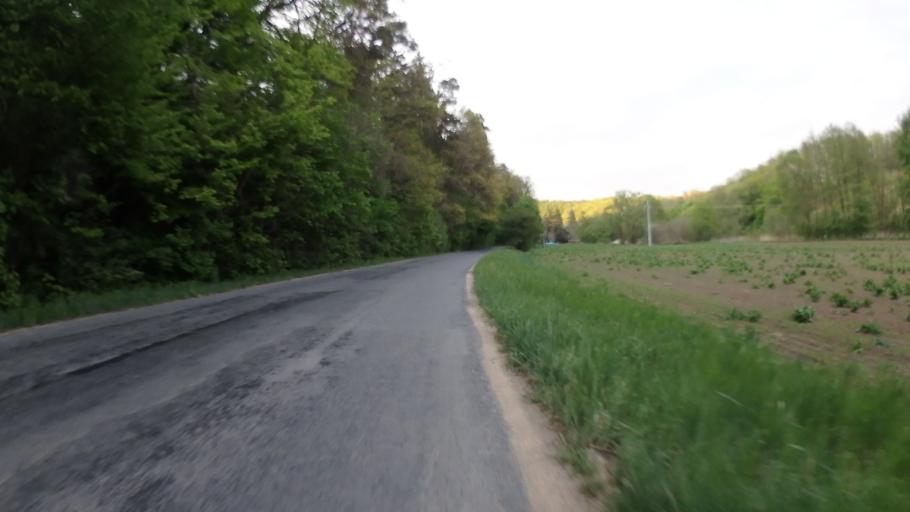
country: CZ
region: South Moravian
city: Strelice
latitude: 49.1412
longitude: 16.4647
